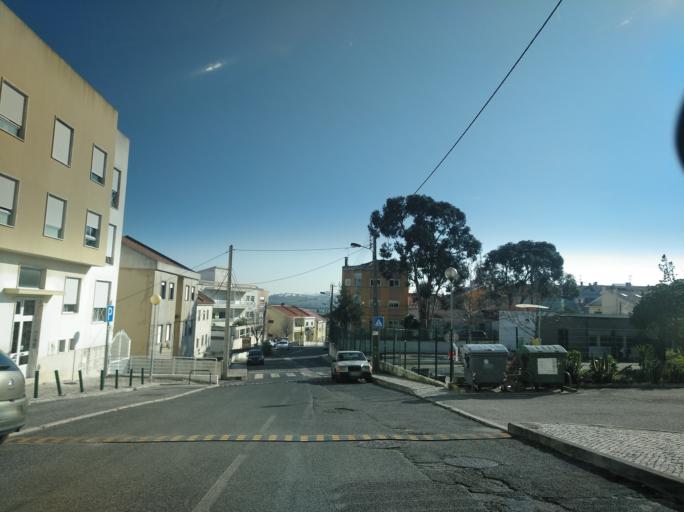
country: PT
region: Lisbon
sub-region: Odivelas
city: Famoes
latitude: 38.7824
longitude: -9.2060
